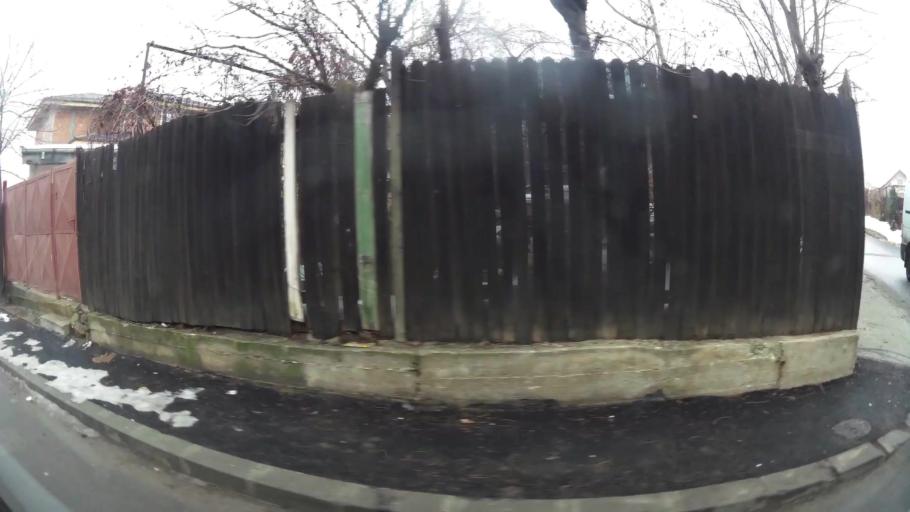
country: RO
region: Ilfov
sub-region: Comuna Popesti-Leordeni
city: Popesti-Leordeni
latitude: 44.4059
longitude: 26.1701
